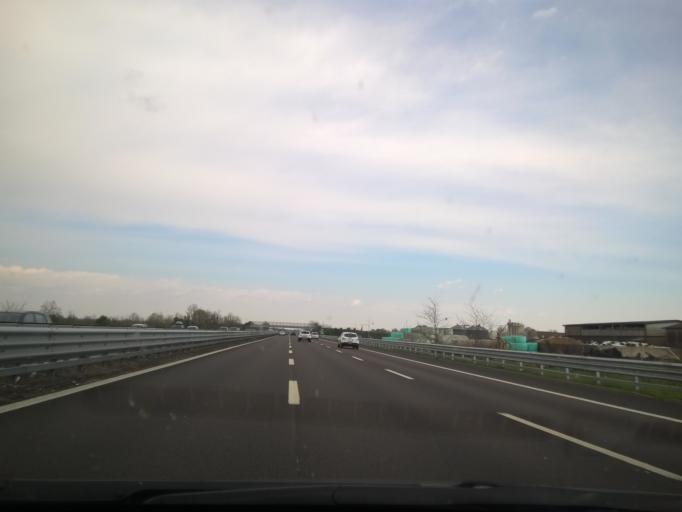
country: IT
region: Lombardy
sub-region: Provincia di Brescia
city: Molinetto
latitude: 45.4763
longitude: 10.3487
